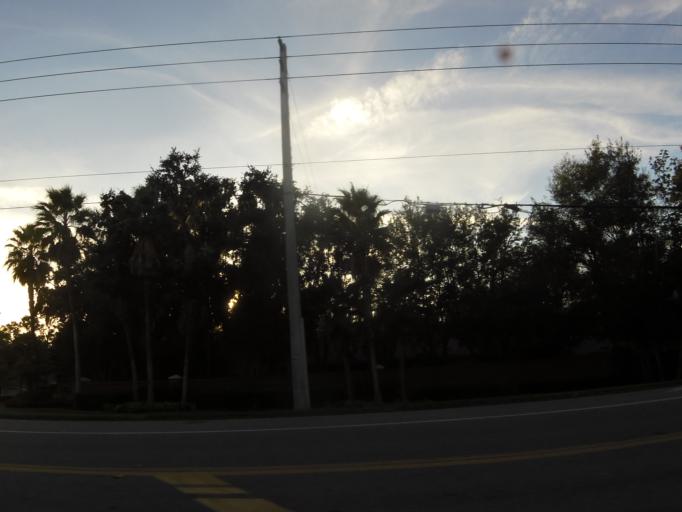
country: US
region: Florida
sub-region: Saint Johns County
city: Palm Valley
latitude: 30.1616
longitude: -81.3856
